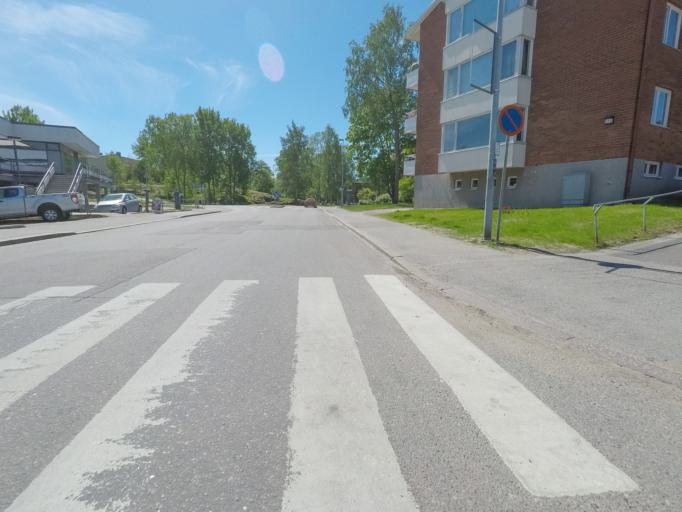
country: FI
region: Uusimaa
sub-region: Helsinki
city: Helsinki
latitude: 60.1867
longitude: 25.0072
